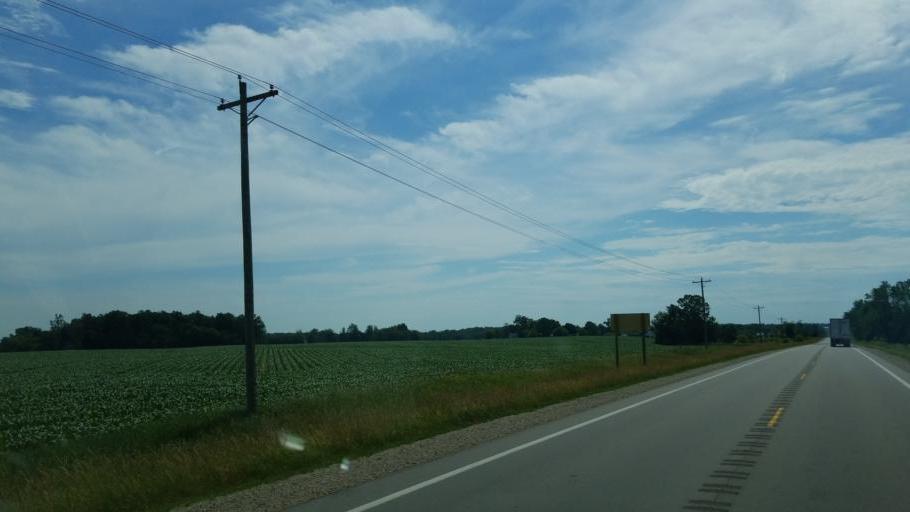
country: US
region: Michigan
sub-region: Eaton County
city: Charlotte
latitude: 42.6470
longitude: -84.8941
